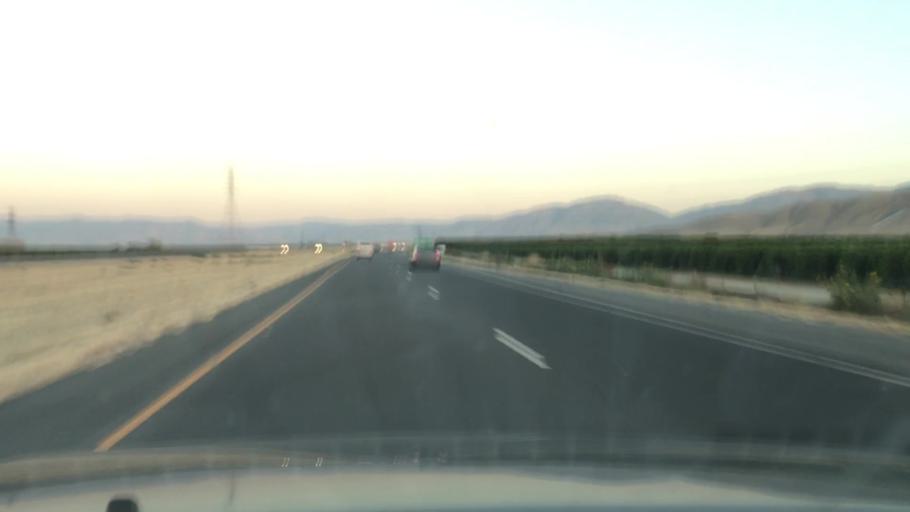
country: US
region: California
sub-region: Kern County
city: Weedpatch
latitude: 35.0516
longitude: -118.9903
